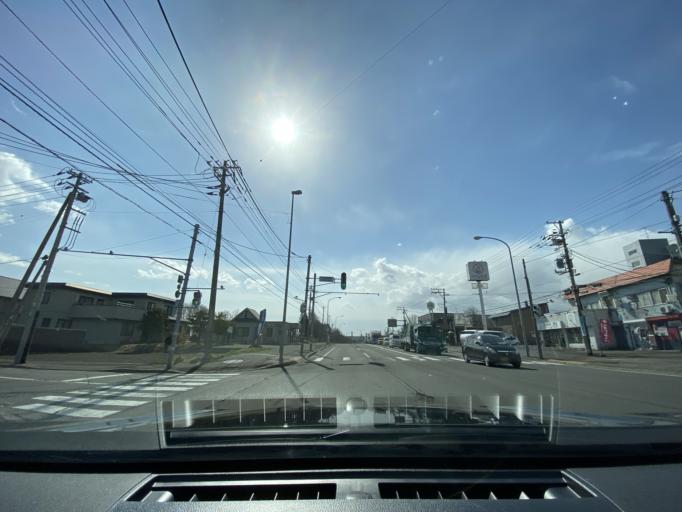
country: JP
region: Hokkaido
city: Kitahiroshima
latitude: 42.9705
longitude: 141.4794
